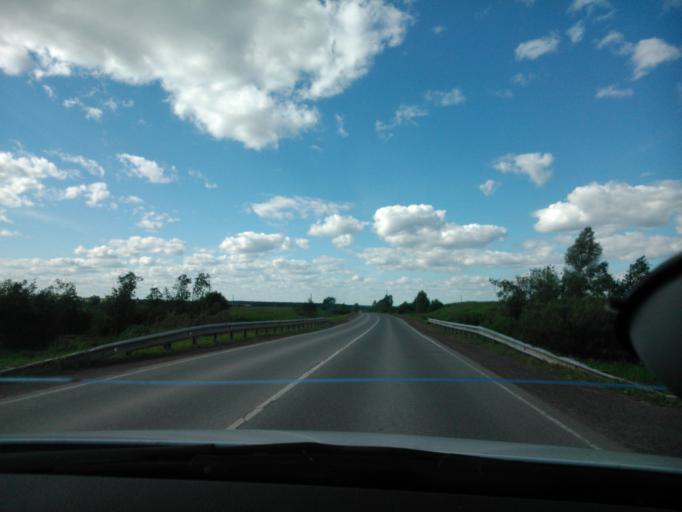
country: RU
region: Perm
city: Ust'-Kachka
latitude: 57.9310
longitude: 55.7611
